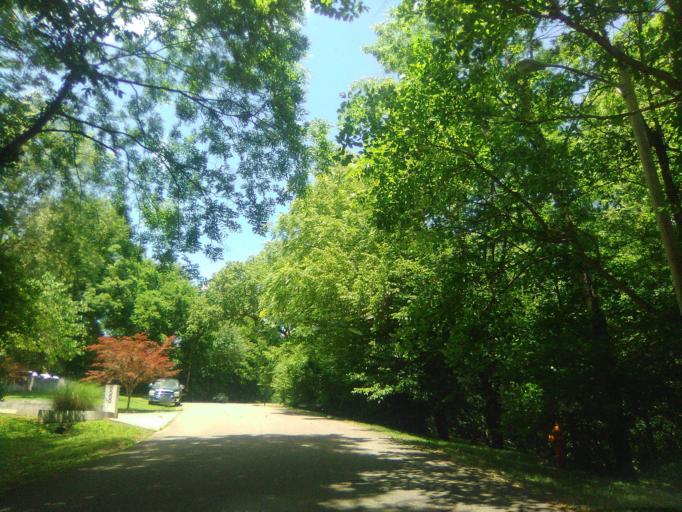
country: US
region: Tennessee
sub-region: Davidson County
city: Belle Meade
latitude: 36.1281
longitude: -86.8699
